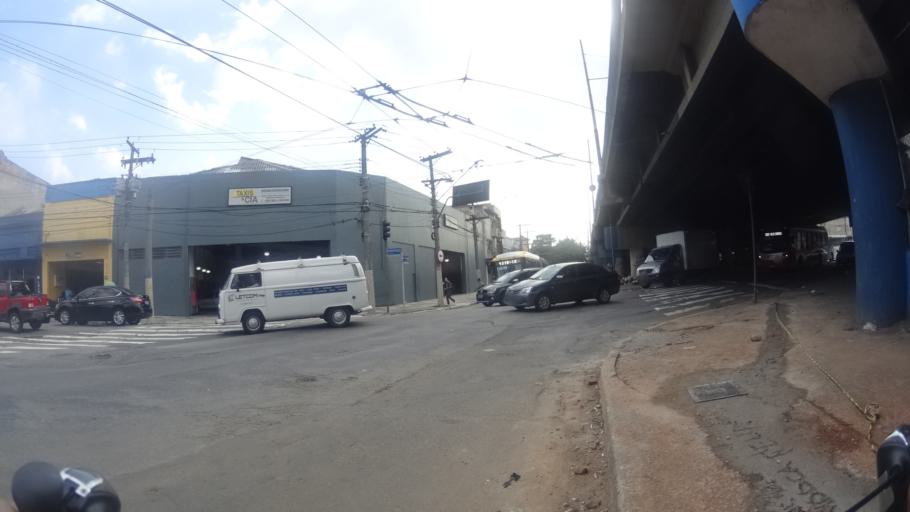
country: BR
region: Sao Paulo
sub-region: Sao Paulo
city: Sao Paulo
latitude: -23.5531
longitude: -46.6154
